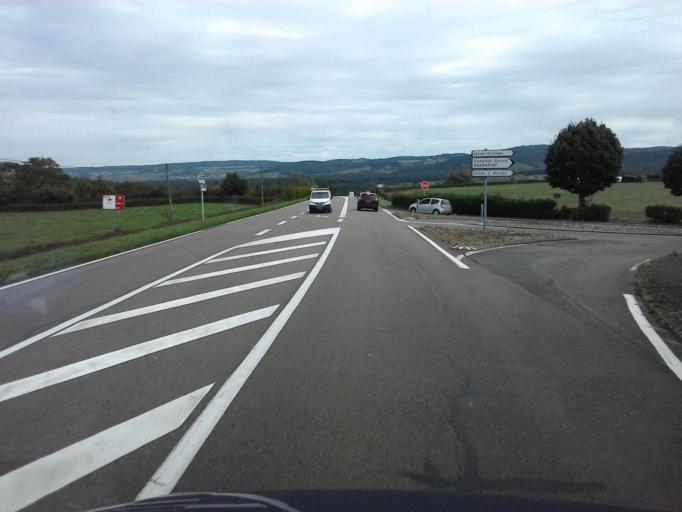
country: FR
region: Bourgogne
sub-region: Departement de Saone-et-Loire
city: Cluny
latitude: 46.4399
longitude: 4.6504
